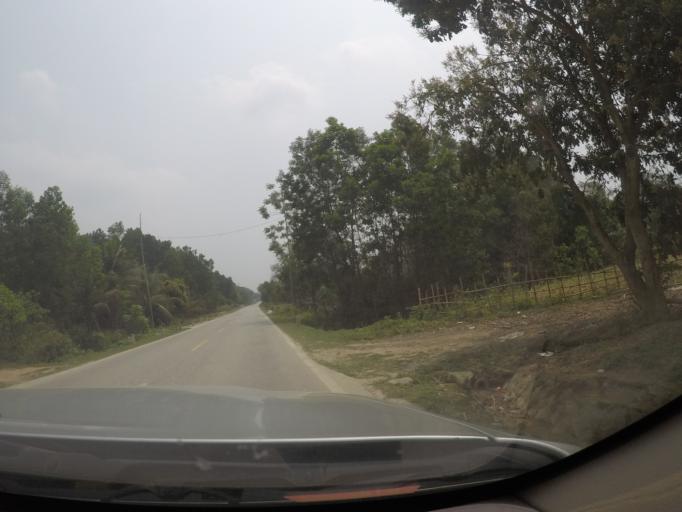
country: VN
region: Thanh Hoa
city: Thi Tran Yen Cat
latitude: 19.7702
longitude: 105.4104
